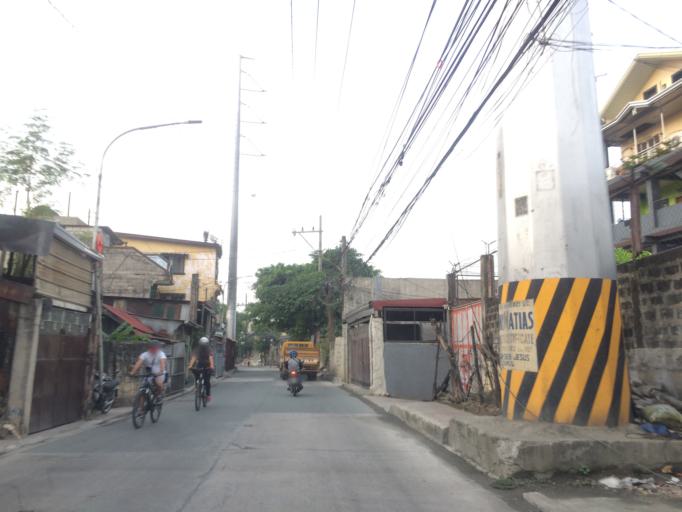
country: PH
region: Calabarzon
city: Del Monte
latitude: 14.6517
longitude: 121.0098
